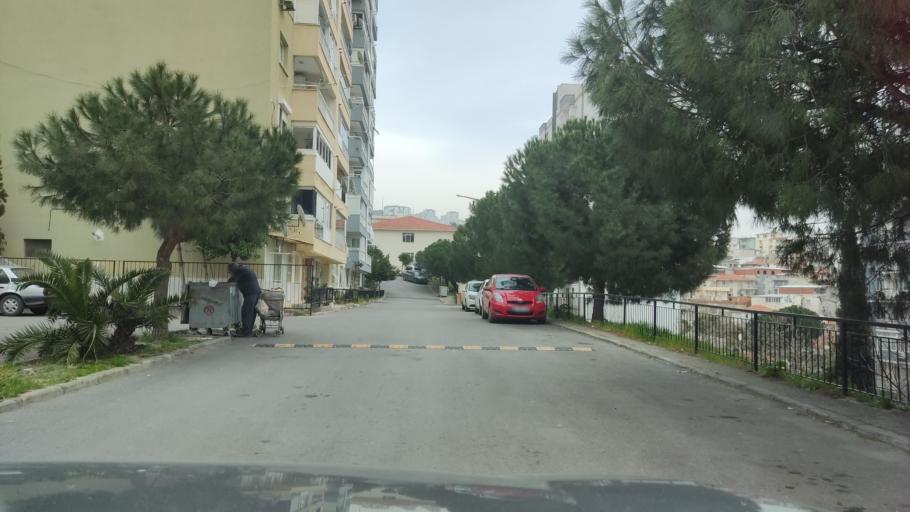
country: TR
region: Izmir
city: Karsiyaka
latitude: 38.5034
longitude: 27.0736
